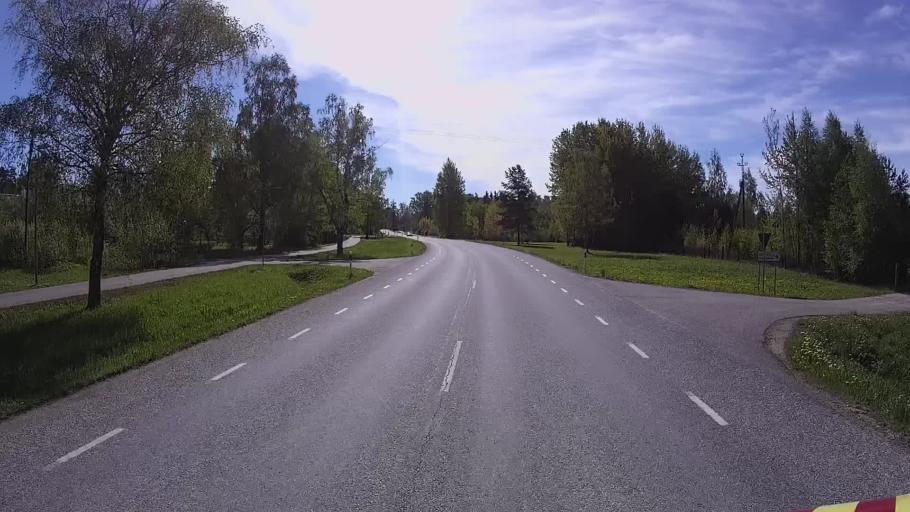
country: EE
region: Polvamaa
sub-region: Raepina vald
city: Rapina
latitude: 58.0864
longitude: 27.4878
